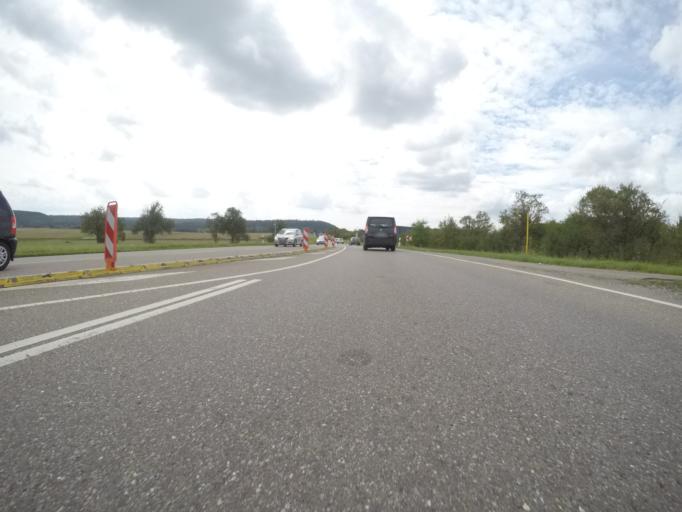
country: DE
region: Baden-Wuerttemberg
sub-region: Regierungsbezirk Stuttgart
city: Gartringen
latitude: 48.6345
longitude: 8.9048
